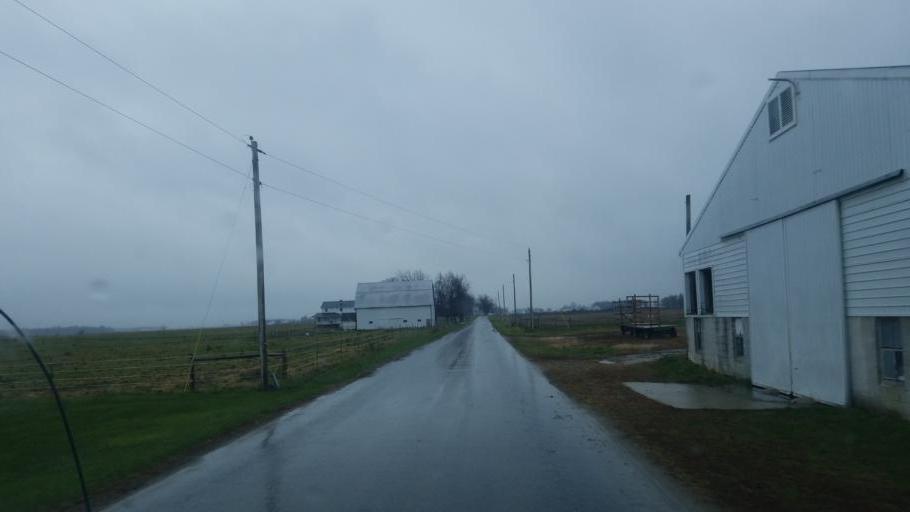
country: US
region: Indiana
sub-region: Adams County
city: Berne
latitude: 40.6407
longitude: -84.8782
